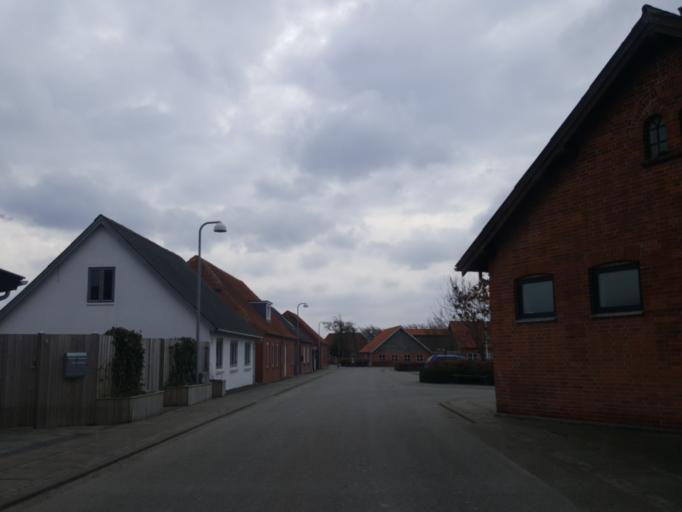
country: DK
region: Central Jutland
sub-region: Lemvig Kommune
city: Lemvig
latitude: 56.4363
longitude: 8.2020
